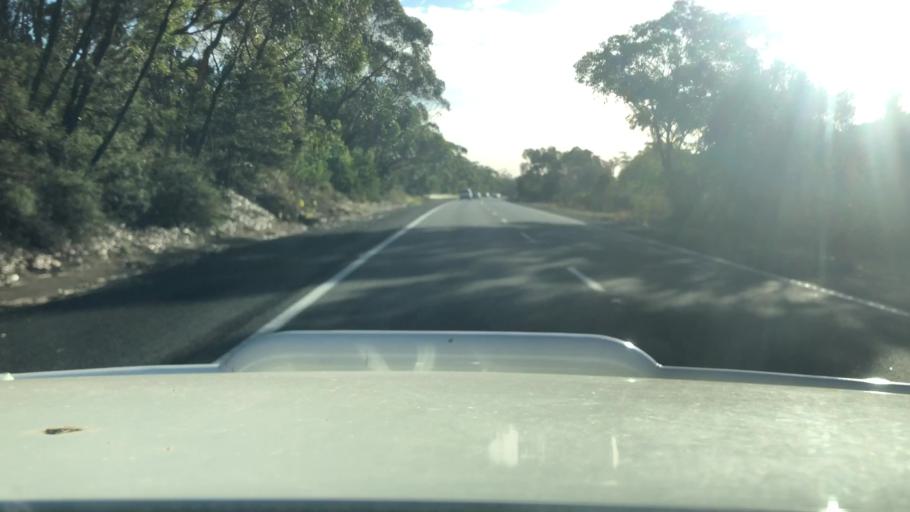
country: AU
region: New South Wales
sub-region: Wollondilly
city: Buxton
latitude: -34.3386
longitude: 150.5561
